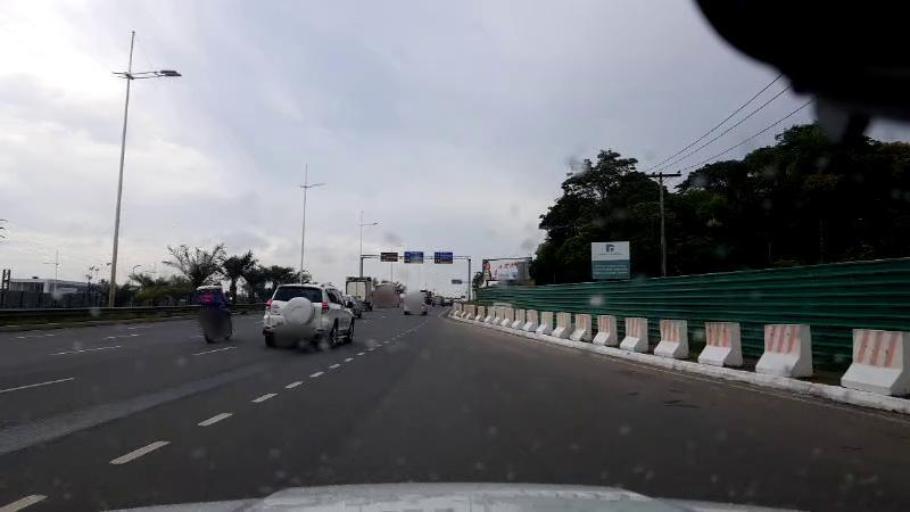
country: BR
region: Bahia
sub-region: Salvador
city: Salvador
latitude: -12.9454
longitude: -38.4219
